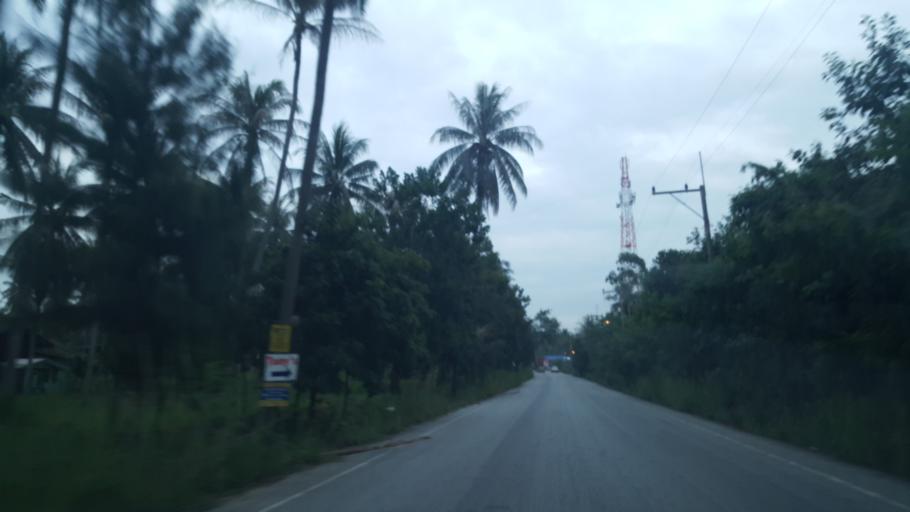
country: TH
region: Chon Buri
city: Bang Lamung
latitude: 12.9838
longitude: 100.9875
